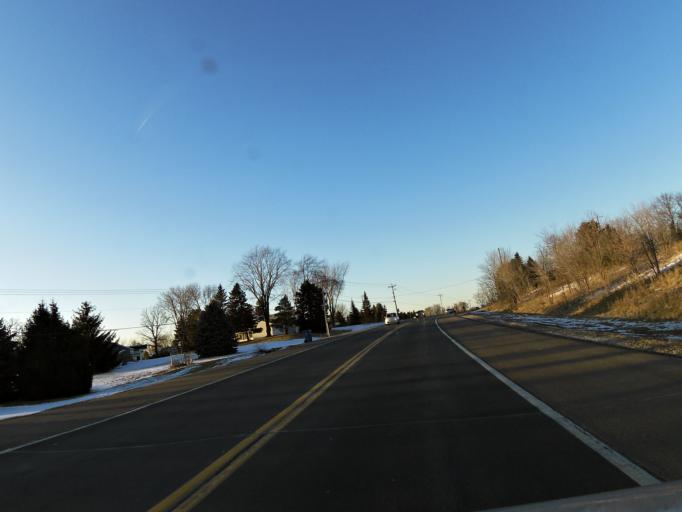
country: US
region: Minnesota
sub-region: Washington County
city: Lake Elmo
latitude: 44.9839
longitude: -92.8624
